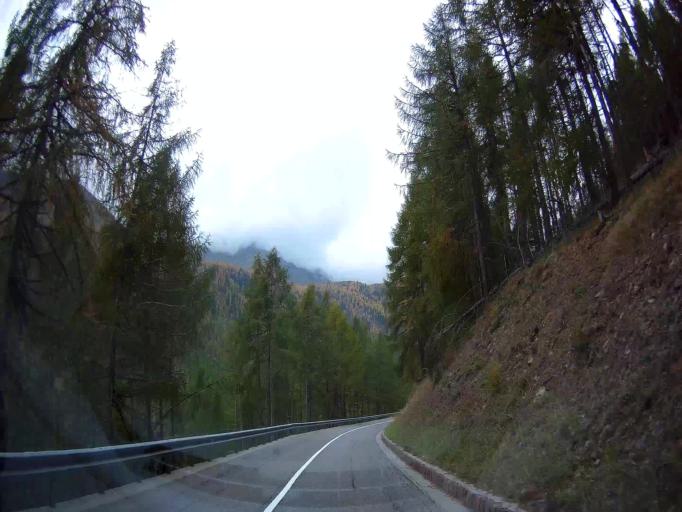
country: IT
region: Trentino-Alto Adige
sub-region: Bolzano
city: Senales
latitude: 46.7370
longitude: 10.8225
